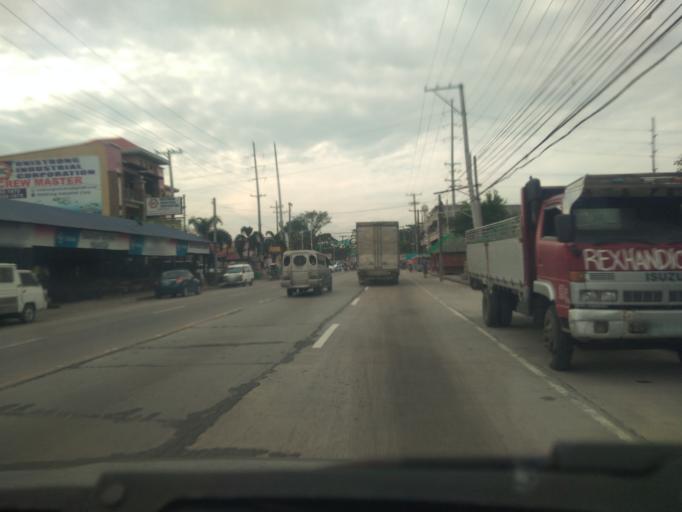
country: PH
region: Central Luzon
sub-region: Province of Pampanga
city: San Fernando
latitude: 15.0257
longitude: 120.6976
